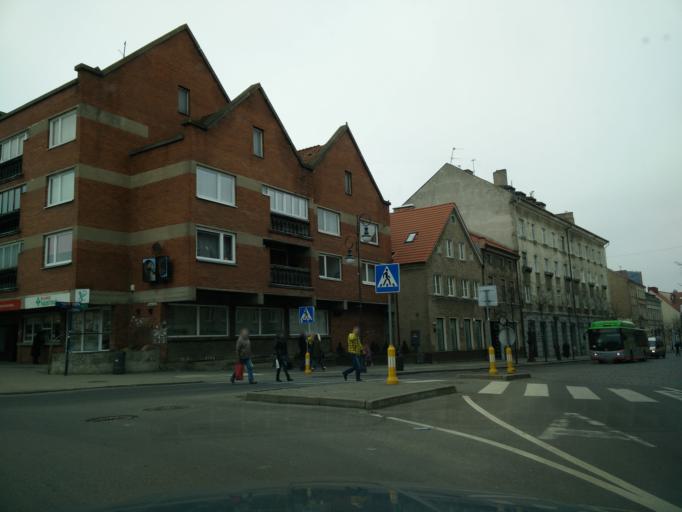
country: LT
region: Klaipedos apskritis
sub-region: Klaipeda
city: Klaipeda
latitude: 55.7070
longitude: 21.1388
